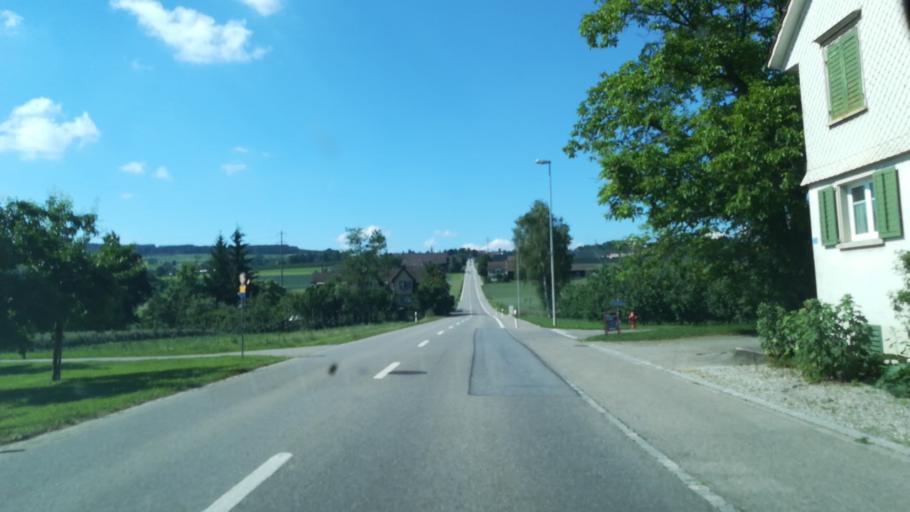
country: CH
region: Thurgau
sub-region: Weinfelden District
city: Berg
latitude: 47.5612
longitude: 9.1734
